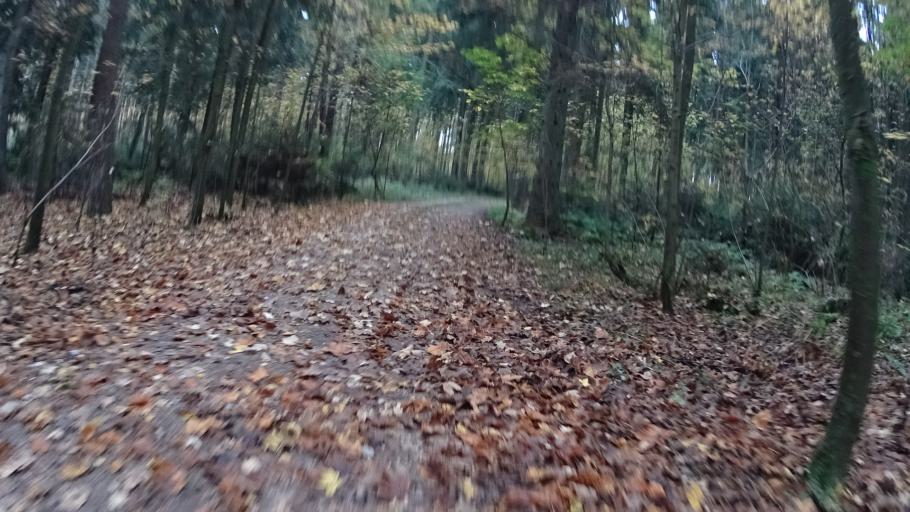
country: DE
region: Bavaria
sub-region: Upper Bavaria
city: Hitzhofen
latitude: 48.8394
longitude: 11.2932
